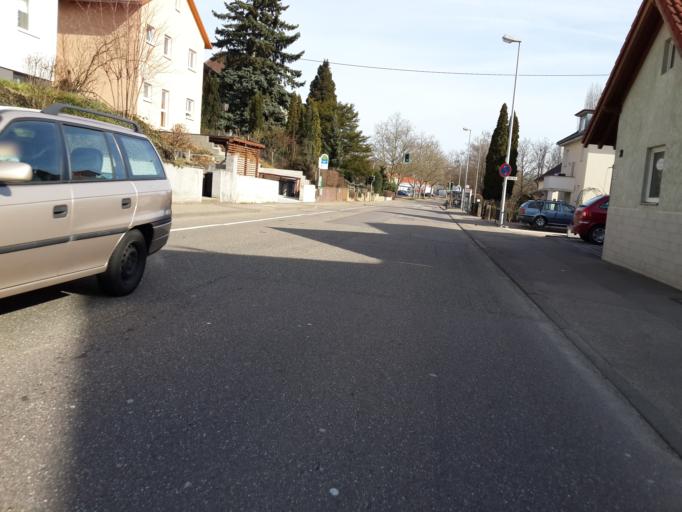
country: DE
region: Baden-Wuerttemberg
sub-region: Regierungsbezirk Stuttgart
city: Heilbronn
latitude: 49.1622
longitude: 9.1746
